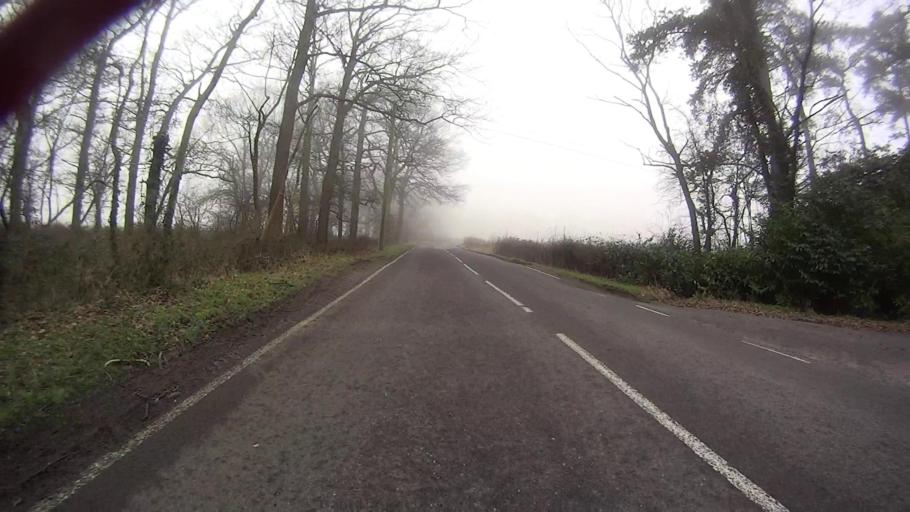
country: GB
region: England
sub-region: Surrey
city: Newdigate
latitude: 51.1405
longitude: -0.3174
